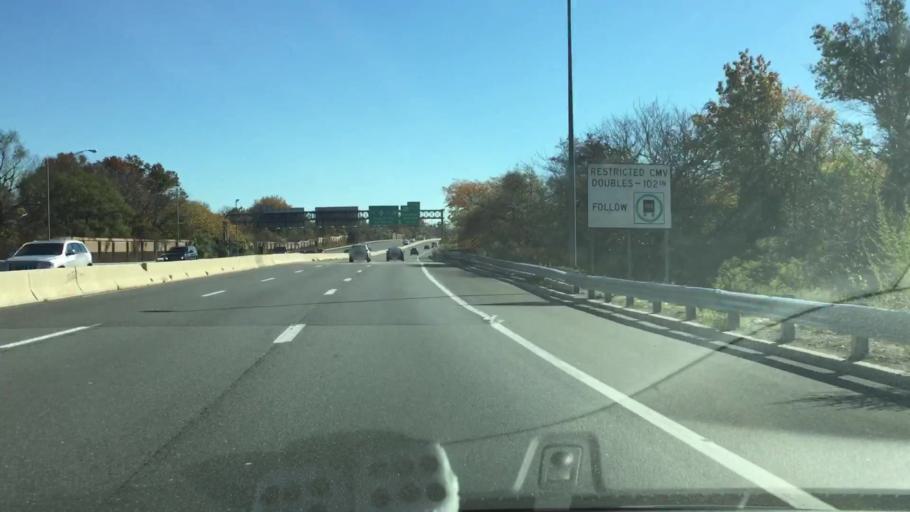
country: US
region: New Jersey
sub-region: Camden County
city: Gloucester City
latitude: 39.8997
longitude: -75.1104
